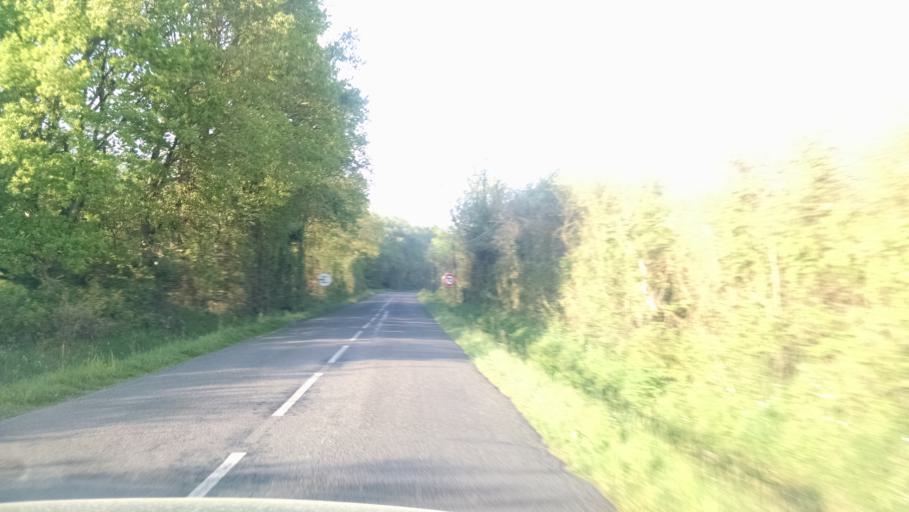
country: FR
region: Pays de la Loire
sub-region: Departement de la Loire-Atlantique
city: Saint-Lumine-de-Clisson
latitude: 47.0729
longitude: -1.3469
